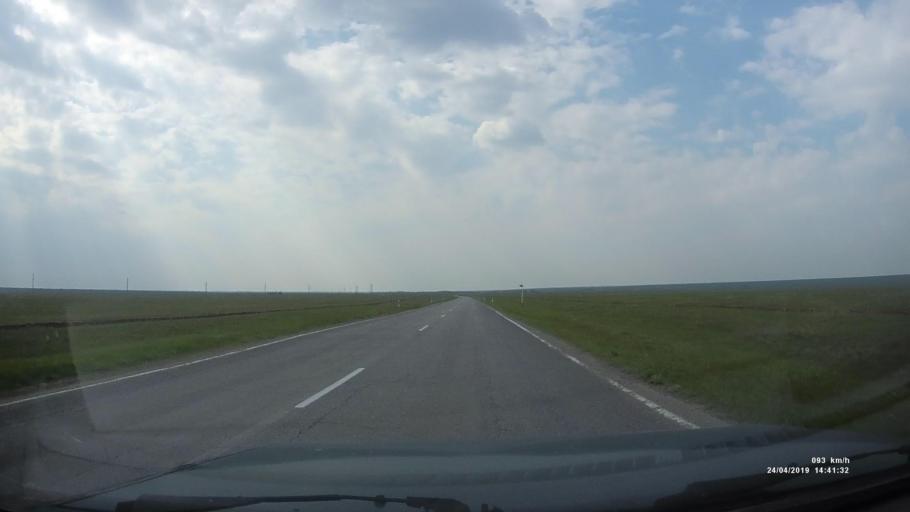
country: RU
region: Rostov
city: Remontnoye
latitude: 46.4459
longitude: 43.8783
